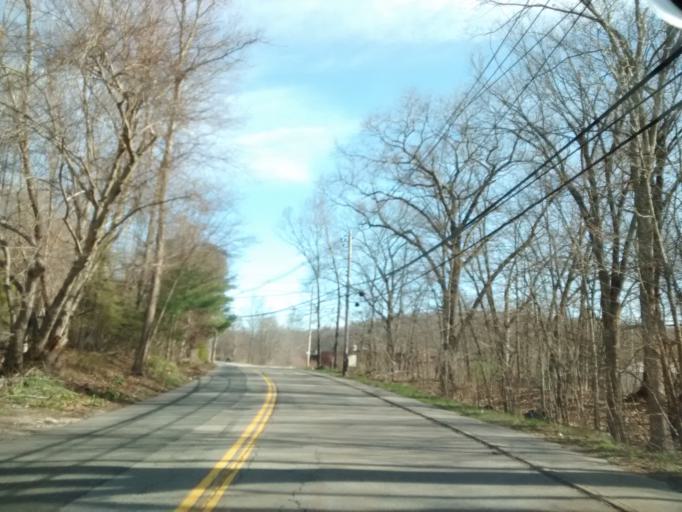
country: US
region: Massachusetts
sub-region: Worcester County
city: Millbury
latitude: 42.1973
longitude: -71.7495
